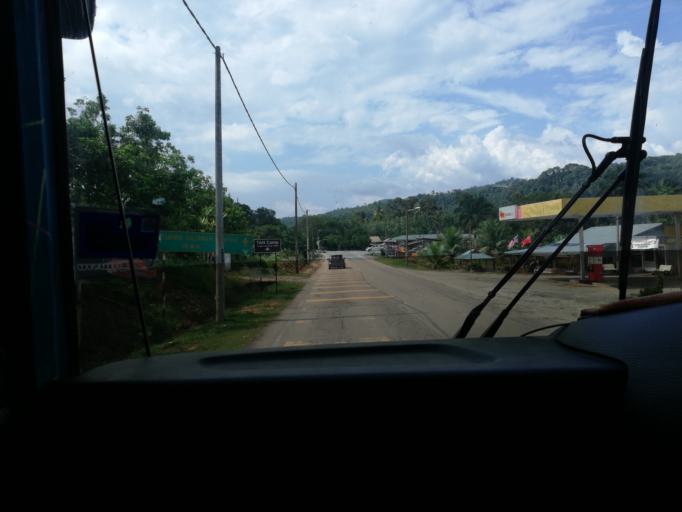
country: MY
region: Kedah
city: Kulim
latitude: 5.2899
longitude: 100.6276
